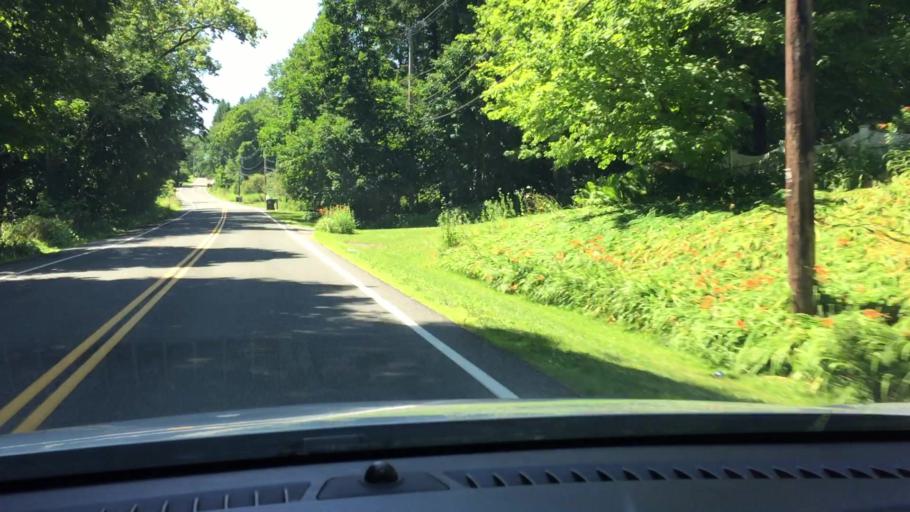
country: US
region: Massachusetts
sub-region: Berkshire County
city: Lenox
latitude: 42.3649
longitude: -73.2597
